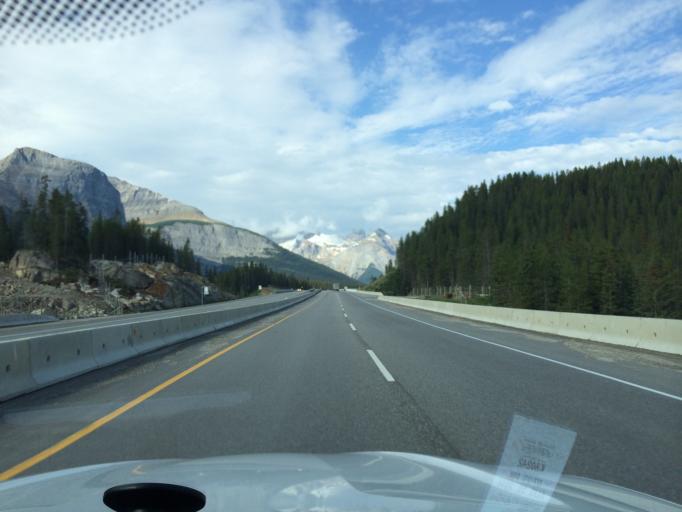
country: CA
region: Alberta
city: Lake Louise
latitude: 51.4572
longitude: -116.2736
